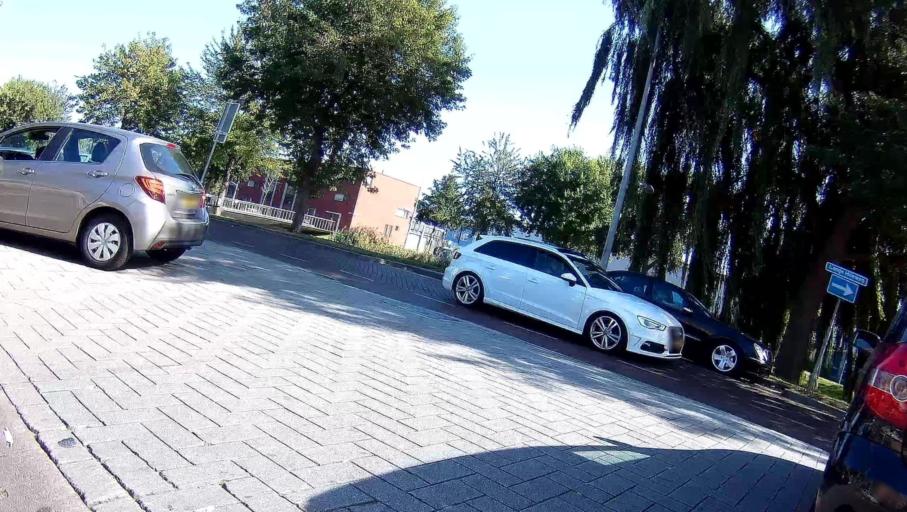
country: NL
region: South Holland
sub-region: Gemeente Rotterdam
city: Rotterdam
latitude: 51.8930
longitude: 4.5012
